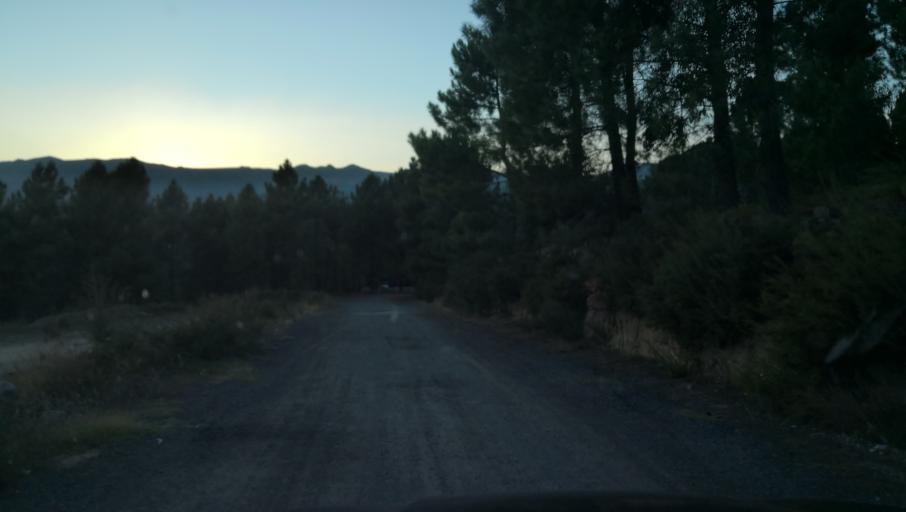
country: PT
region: Vila Real
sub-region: Vila Real
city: Vila Real
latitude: 41.3116
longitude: -7.7699
